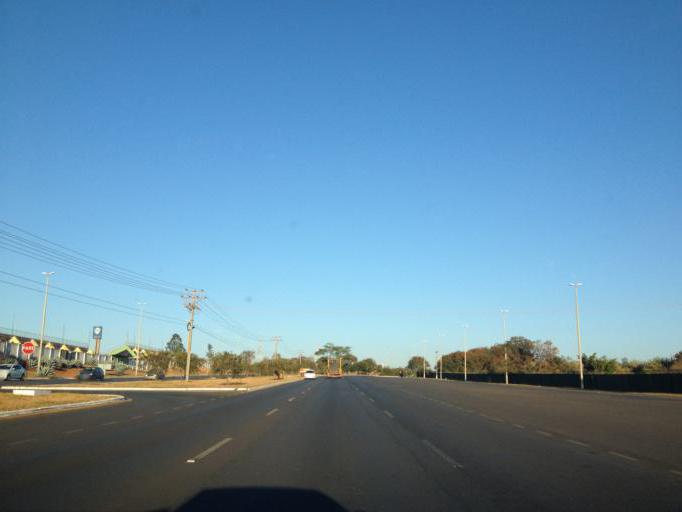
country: BR
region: Federal District
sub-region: Brasilia
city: Brasilia
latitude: -15.7718
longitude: -47.9002
